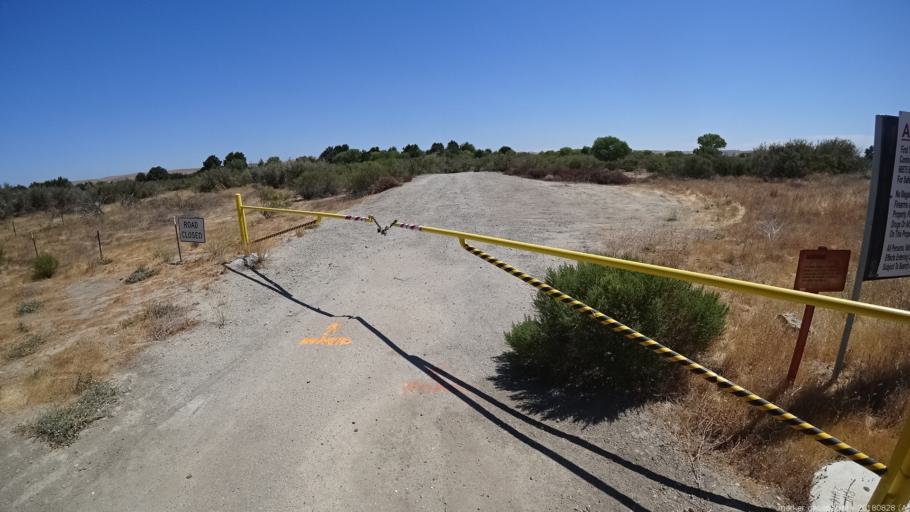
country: US
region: California
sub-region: San Luis Obispo County
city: Lake Nacimiento
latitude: 35.9680
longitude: -120.8910
